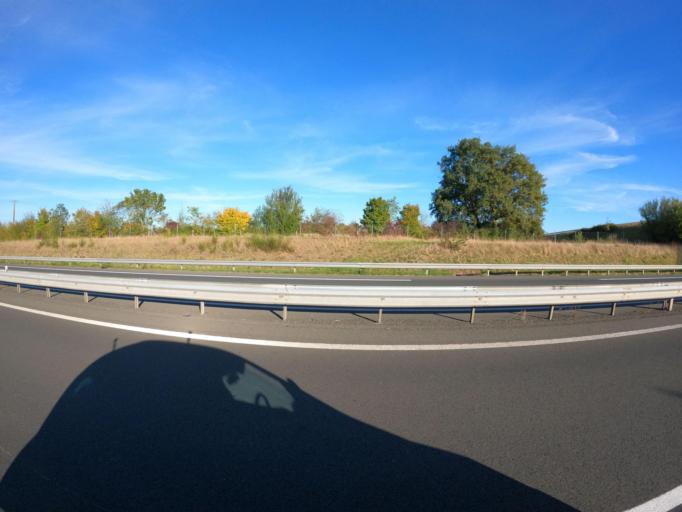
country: FR
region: Pays de la Loire
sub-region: Departement de Maine-et-Loire
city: Saint-Lambert-du-Lattay
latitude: 47.2672
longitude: -0.6142
